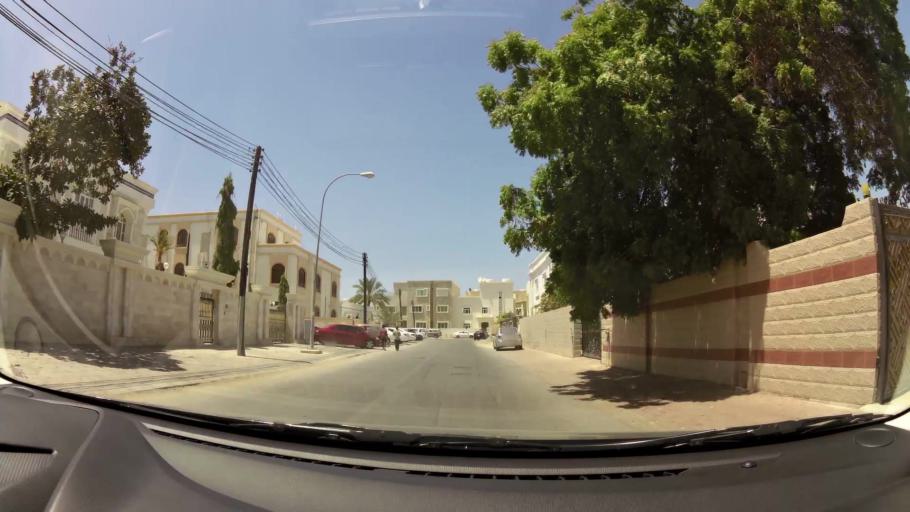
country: OM
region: Muhafazat Masqat
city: Bawshar
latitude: 23.5970
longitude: 58.3819
